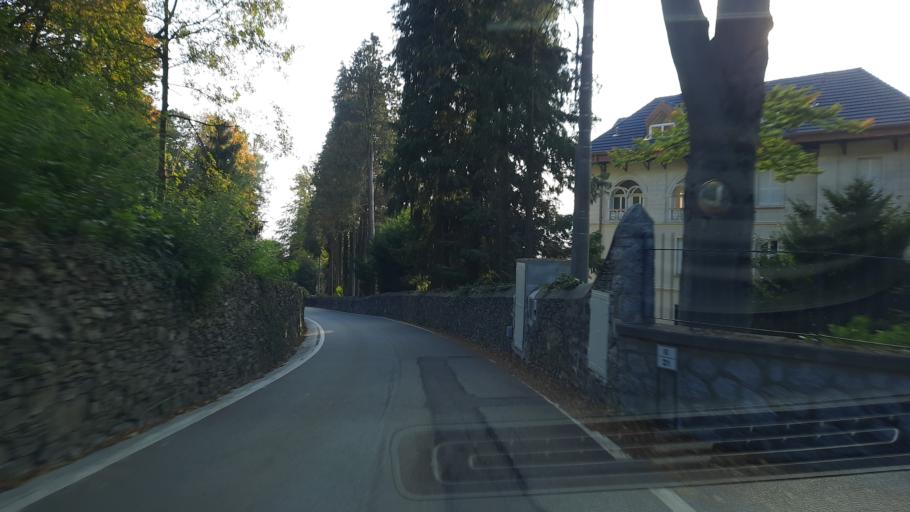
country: IT
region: Piedmont
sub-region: Provincia di Novara
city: Miasino
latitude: 45.8009
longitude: 8.4278
